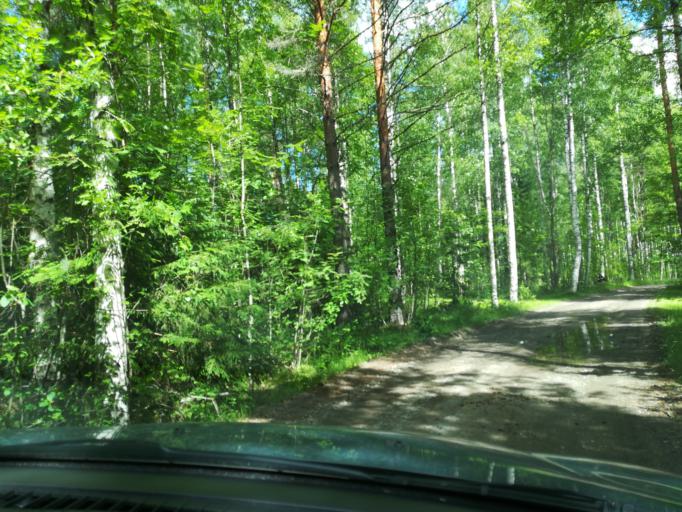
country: FI
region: Southern Savonia
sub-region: Mikkeli
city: Hirvensalmi
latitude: 61.6518
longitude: 26.7790
